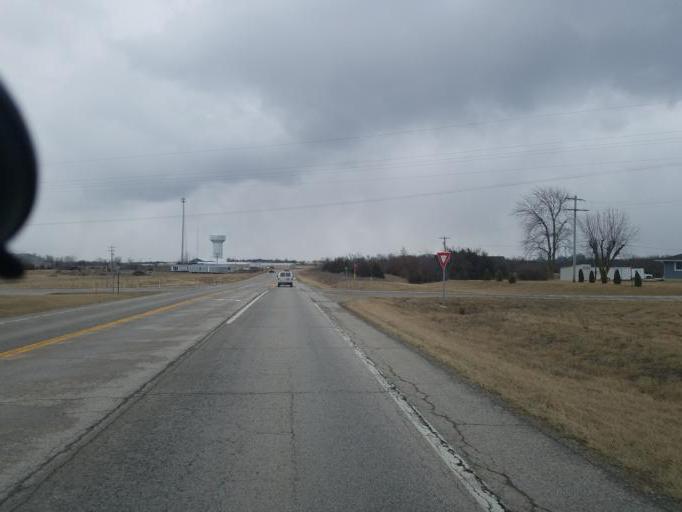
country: US
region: Missouri
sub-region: Macon County
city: Macon
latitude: 39.7670
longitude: -92.4700
